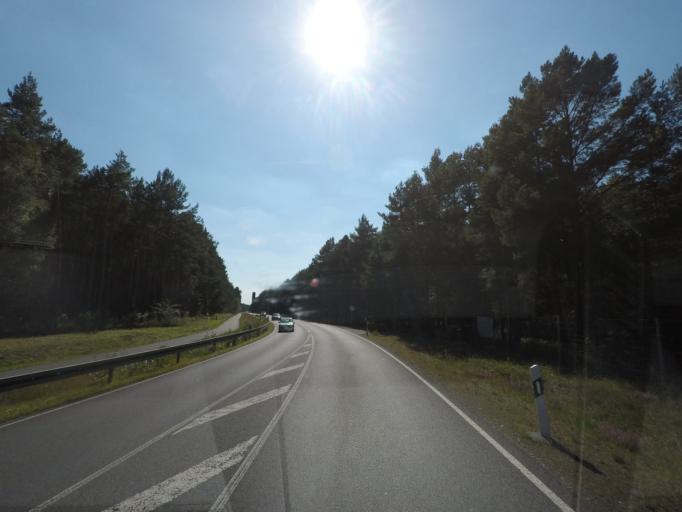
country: DE
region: Brandenburg
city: Schipkau
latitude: 51.5023
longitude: 13.8993
